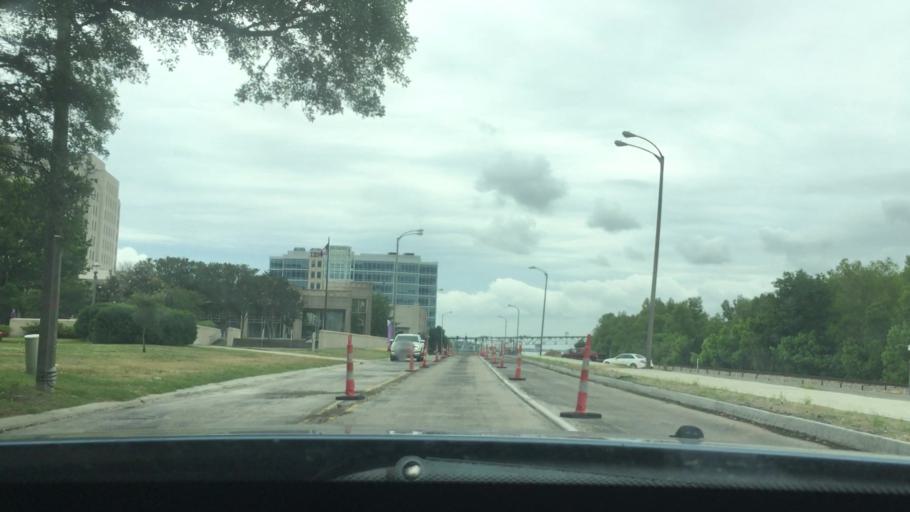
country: US
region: Louisiana
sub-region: West Baton Rouge Parish
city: Port Allen
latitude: 30.4554
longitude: -91.1901
